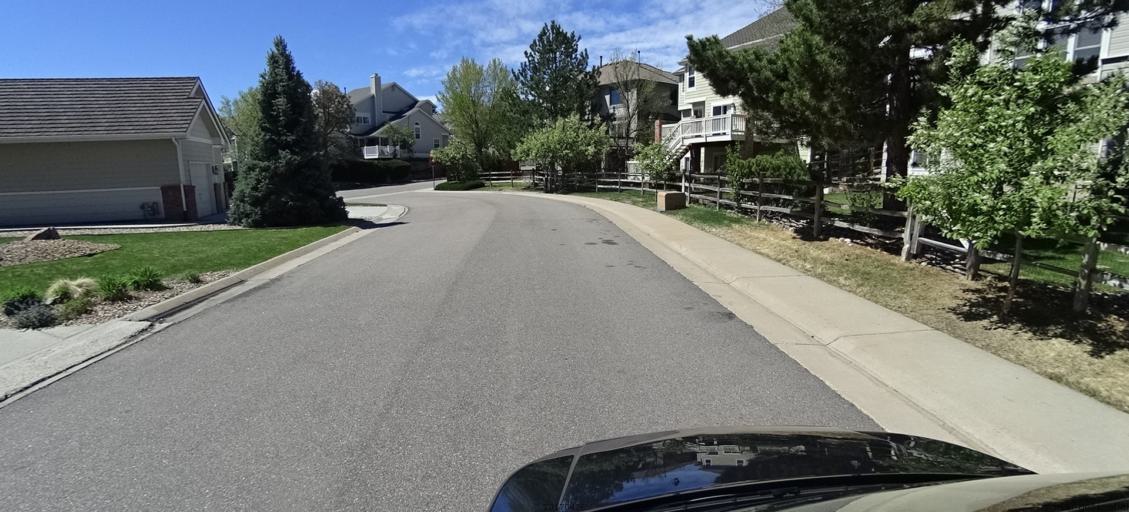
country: US
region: Colorado
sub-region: Adams County
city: Lone Tree
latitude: 39.5473
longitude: -104.8917
